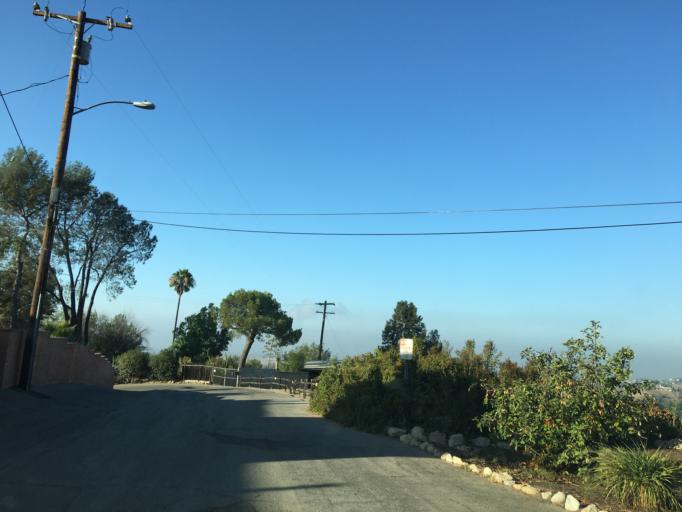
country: US
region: California
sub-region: Los Angeles County
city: San Fernando
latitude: 34.2851
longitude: -118.3771
